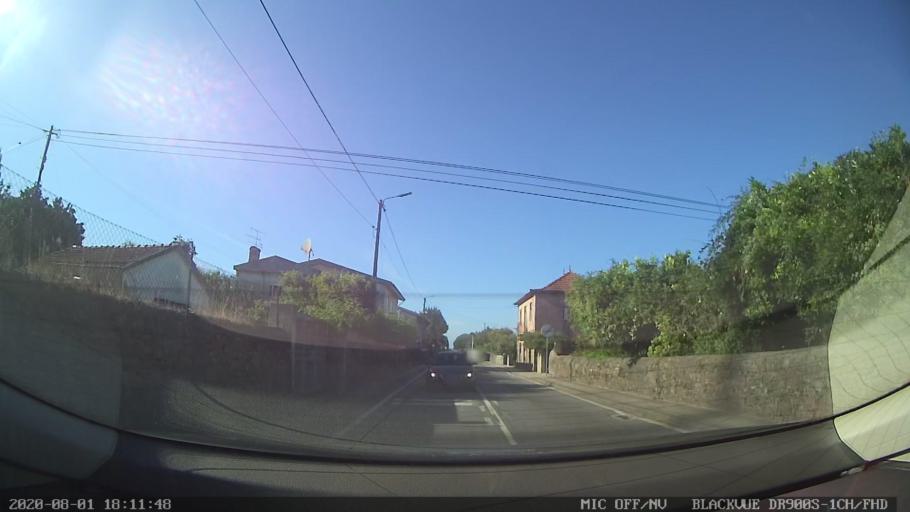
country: PT
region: Porto
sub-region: Santo Tirso
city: Sao Miguel do Couto
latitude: 41.2947
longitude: -8.4710
